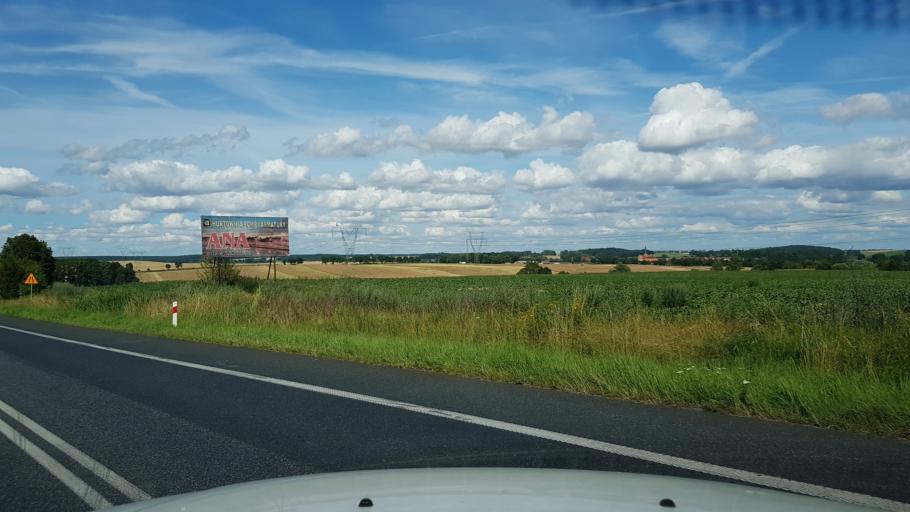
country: PL
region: West Pomeranian Voivodeship
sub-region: Powiat gryfinski
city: Stare Czarnowo
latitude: 53.2962
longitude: 14.7893
